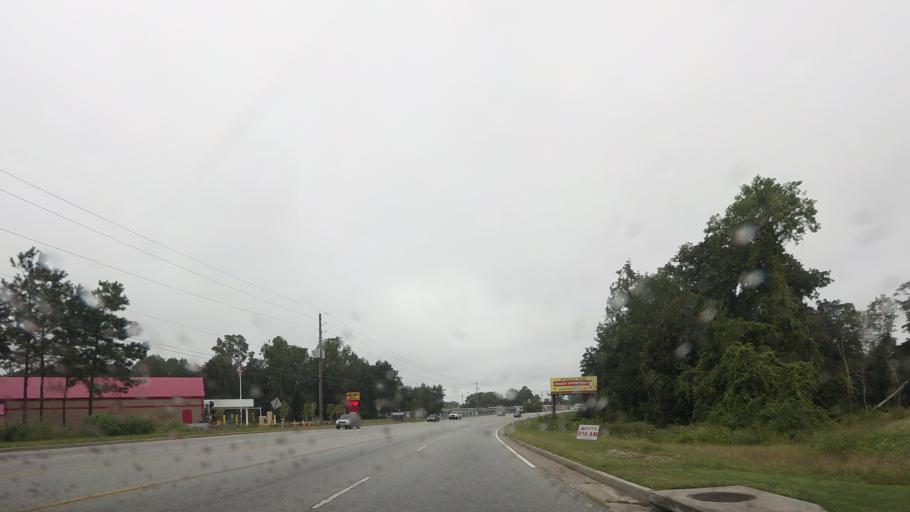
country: US
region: Georgia
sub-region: Lowndes County
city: Remerton
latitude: 30.8313
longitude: -83.3204
